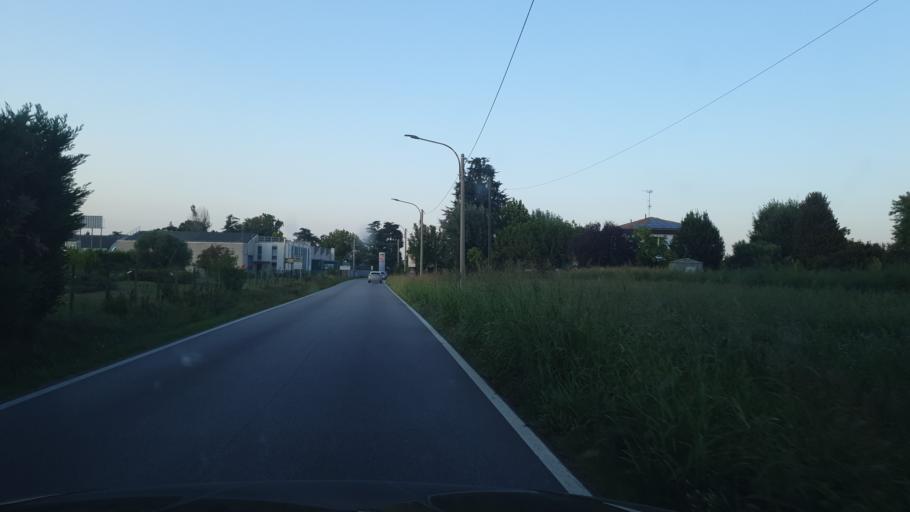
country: IT
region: Emilia-Romagna
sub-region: Provincia di Bologna
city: Quarto Inferiore
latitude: 44.5404
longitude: 11.3939
